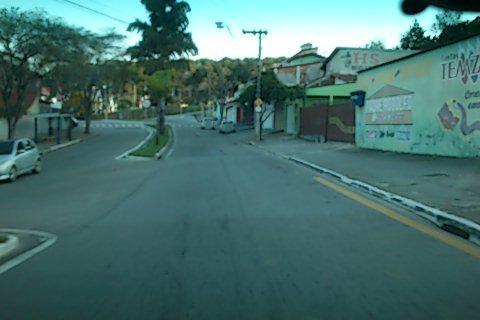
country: BR
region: Sao Paulo
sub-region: Sao Jose Dos Campos
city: Sao Jose dos Campos
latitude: -23.1615
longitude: -45.9105
